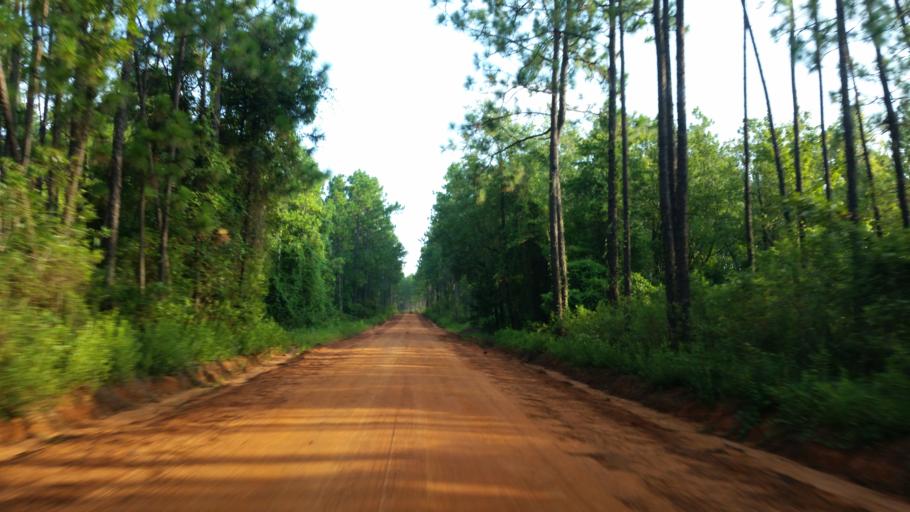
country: US
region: Alabama
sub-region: Escambia County
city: Atmore
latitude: 30.9452
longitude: -87.5711
